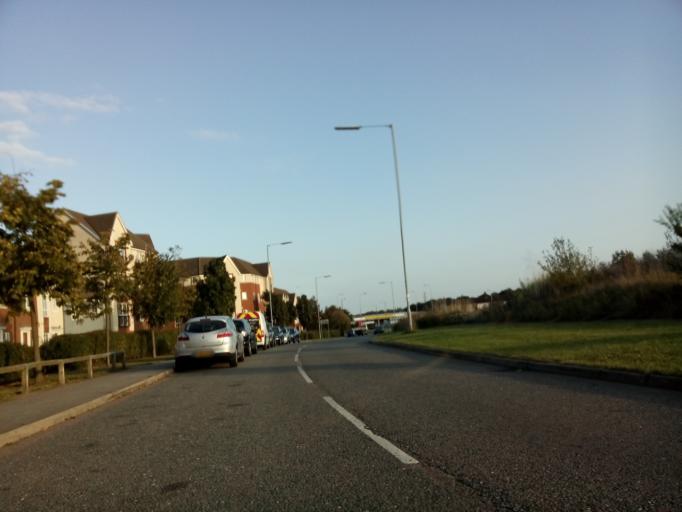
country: GB
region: England
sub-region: Suffolk
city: Bramford
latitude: 52.0662
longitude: 1.1170
